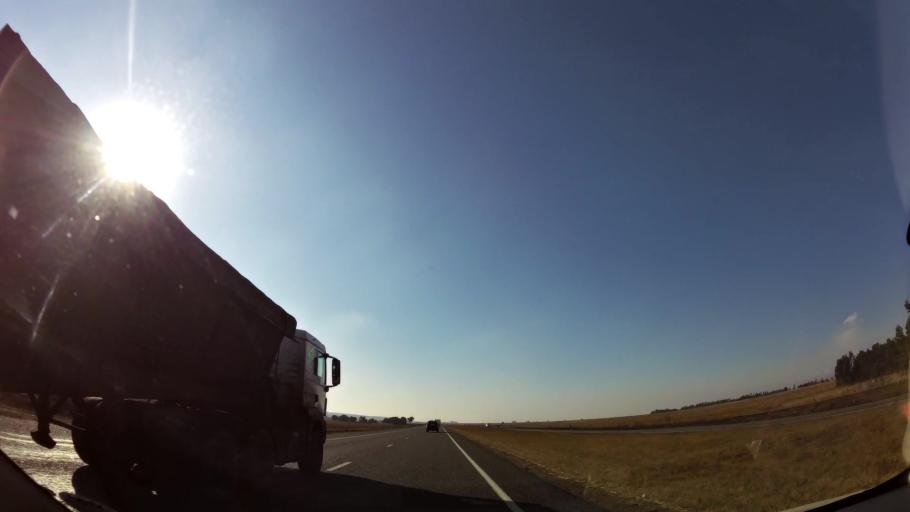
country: ZA
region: Mpumalanga
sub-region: Nkangala District Municipality
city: Delmas
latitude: -26.0190
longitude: 28.9185
